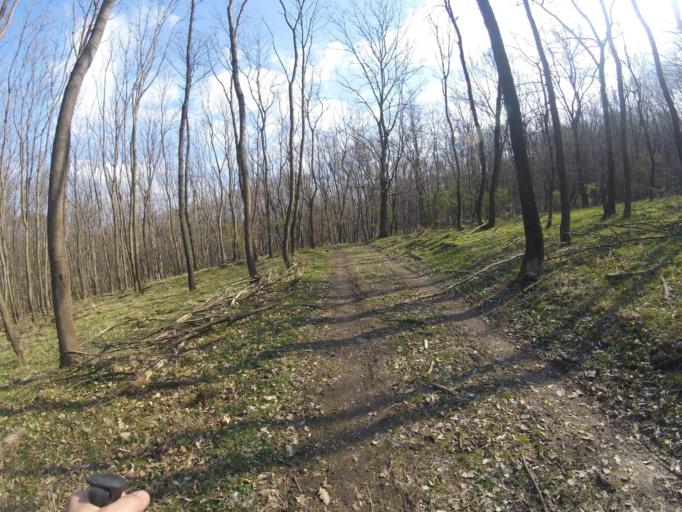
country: HU
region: Komarom-Esztergom
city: Oroszlany
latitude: 47.4124
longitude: 18.3159
